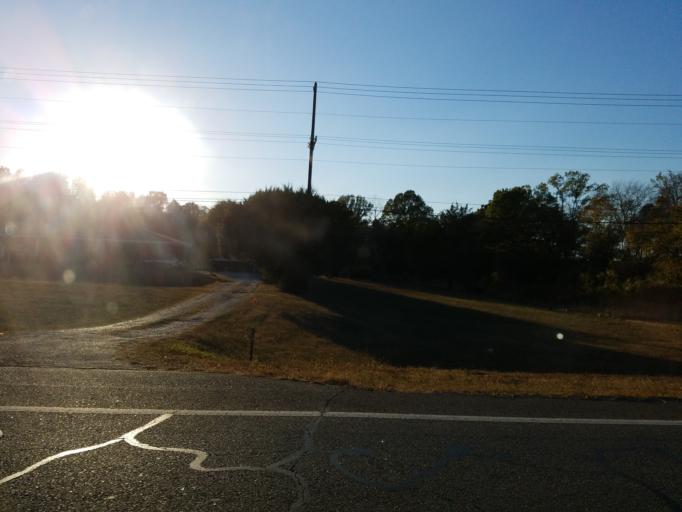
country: US
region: Georgia
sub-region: Bartow County
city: Adairsville
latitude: 34.4275
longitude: -84.9342
